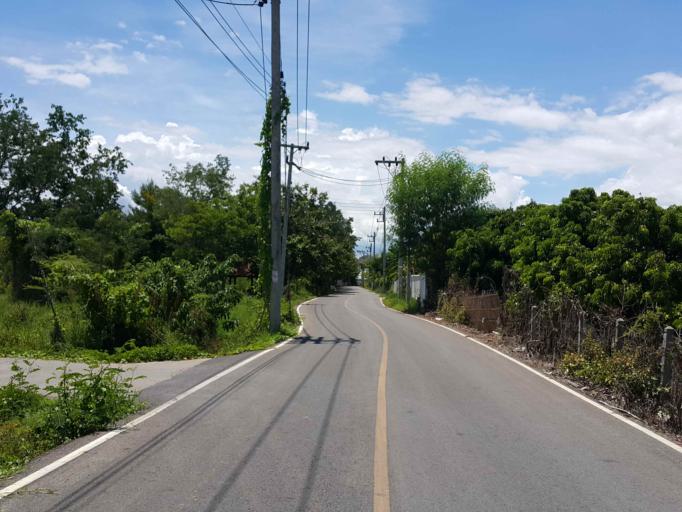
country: TH
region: Chiang Mai
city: Saraphi
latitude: 18.7447
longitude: 99.0039
